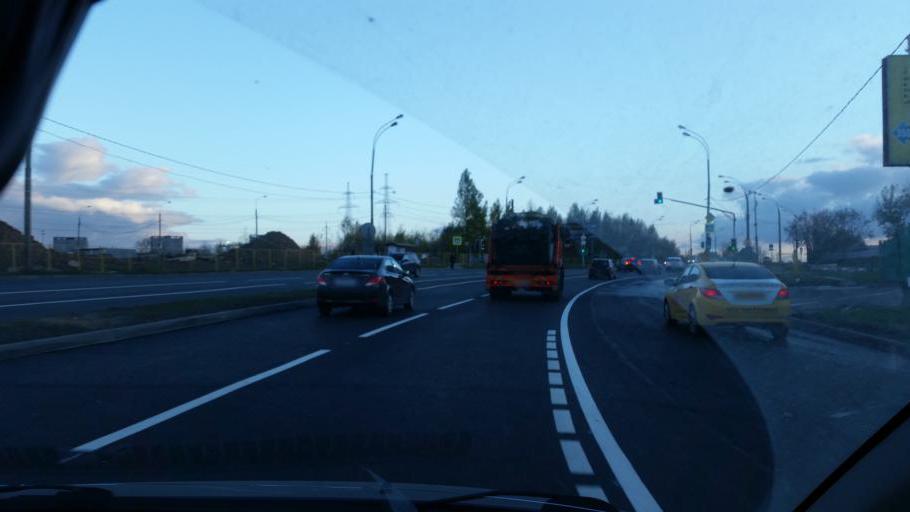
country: RU
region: Moskovskaya
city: Biryulevo Zapadnoye
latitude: 55.6028
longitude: 37.6367
